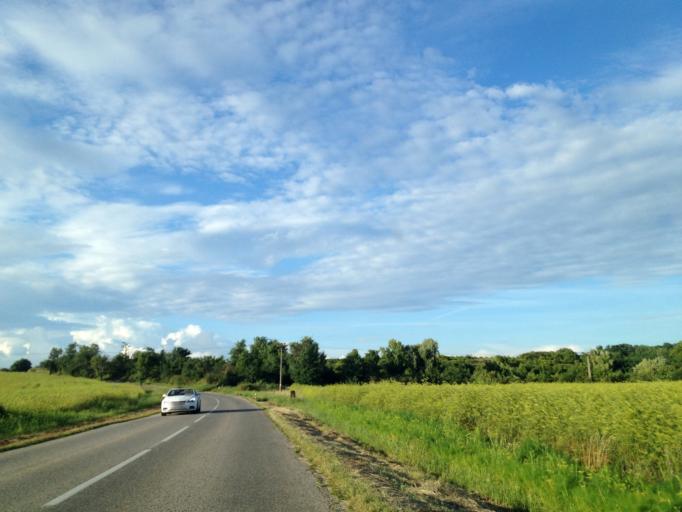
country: SK
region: Nitriansky
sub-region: Okres Komarno
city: Hurbanovo
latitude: 47.8814
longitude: 18.2893
